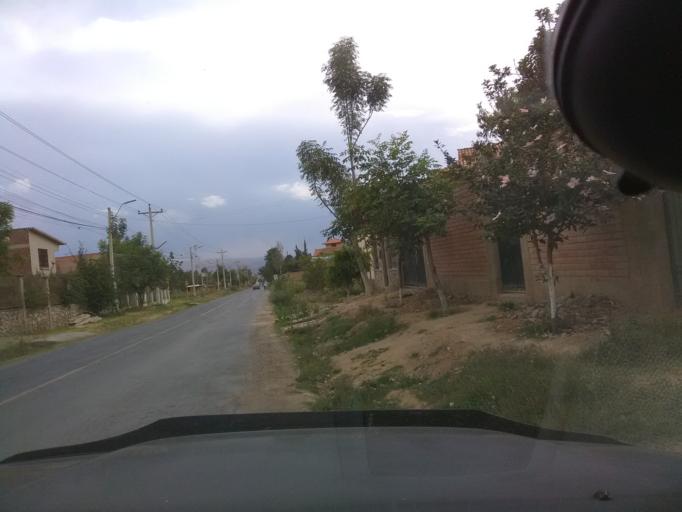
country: BO
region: Cochabamba
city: Cochabamba
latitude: -17.3527
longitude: -66.2261
